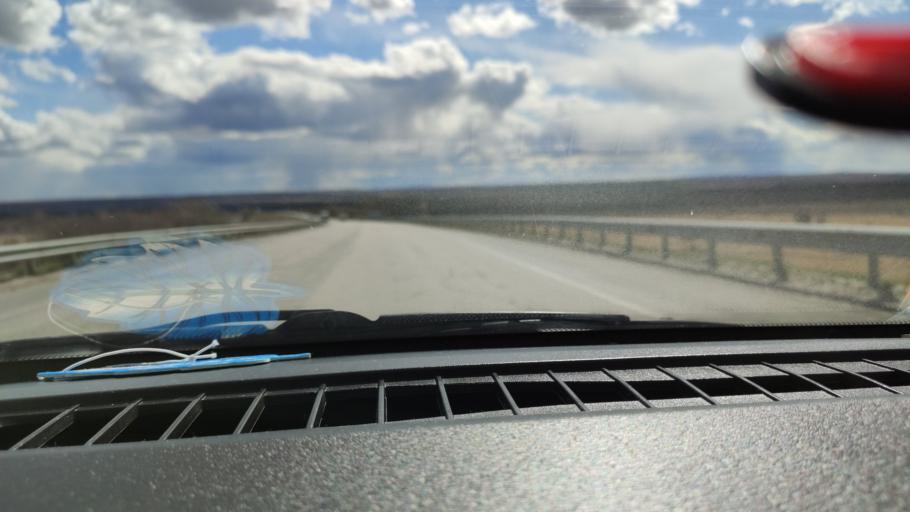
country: RU
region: Samara
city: Varlamovo
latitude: 53.1667
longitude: 48.2812
